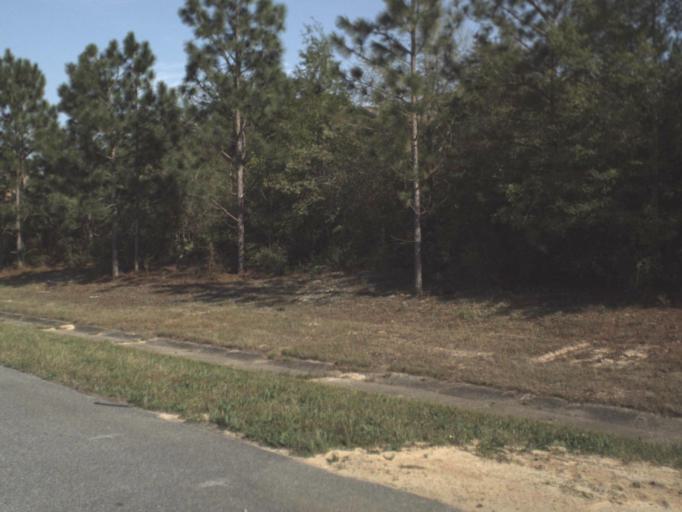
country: US
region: Florida
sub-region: Okaloosa County
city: Crestview
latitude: 30.7169
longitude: -86.6078
